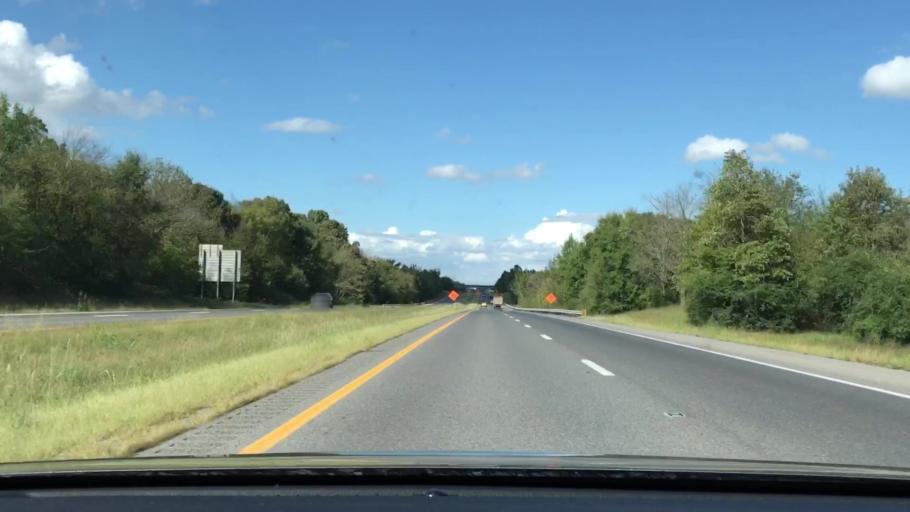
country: US
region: Kentucky
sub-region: Marshall County
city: Calvert City
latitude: 36.9603
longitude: -88.3486
